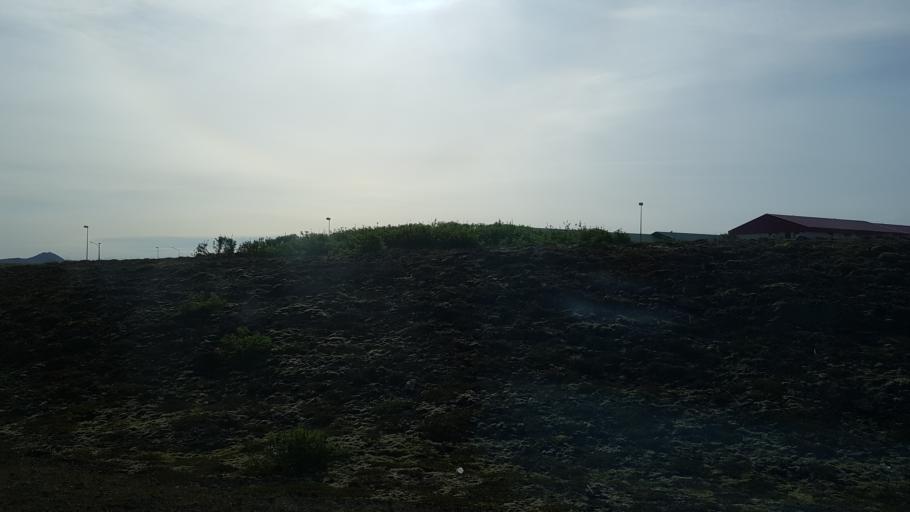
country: IS
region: Southern Peninsula
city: Reykjanesbaer
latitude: 63.9737
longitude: -22.5515
